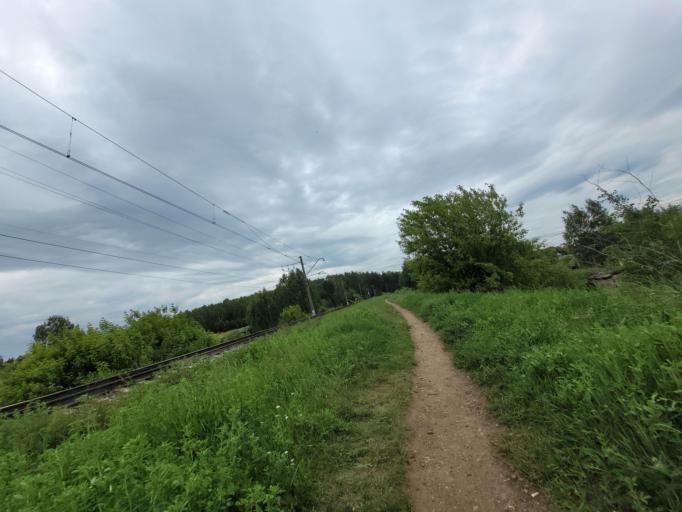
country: RU
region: Moskovskaya
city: Lesnyye Polyany
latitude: 55.9530
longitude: 37.8540
